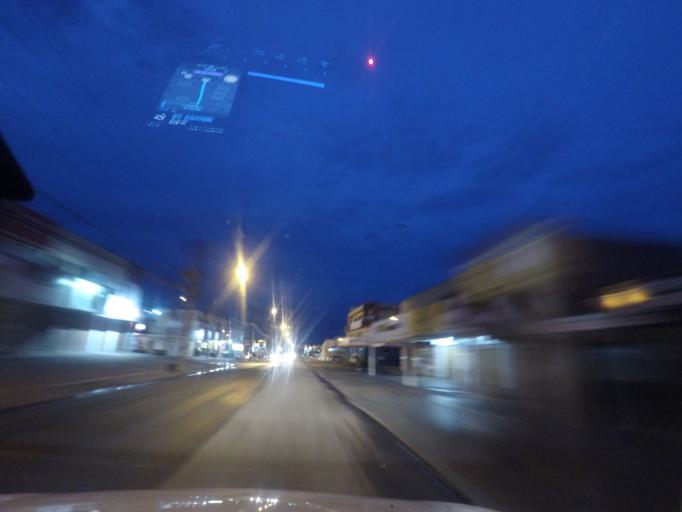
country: BR
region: Goias
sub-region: Goiania
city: Goiania
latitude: -16.7082
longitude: -49.3245
